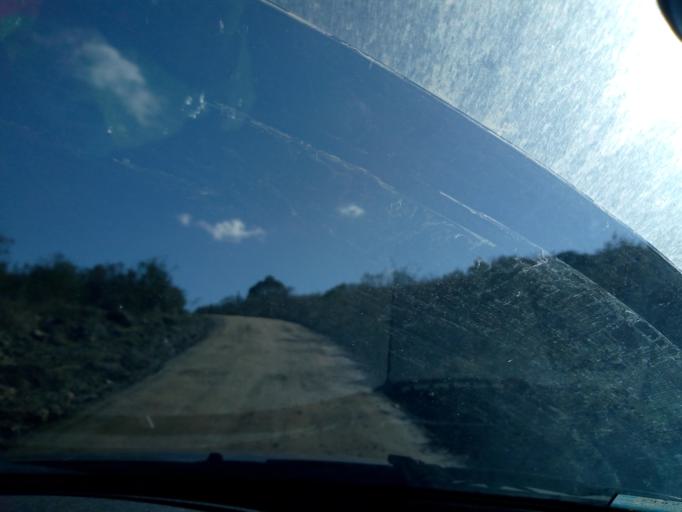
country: AR
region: Buenos Aires
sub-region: Partido de Tandil
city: Tandil
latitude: -37.3650
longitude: -59.1381
